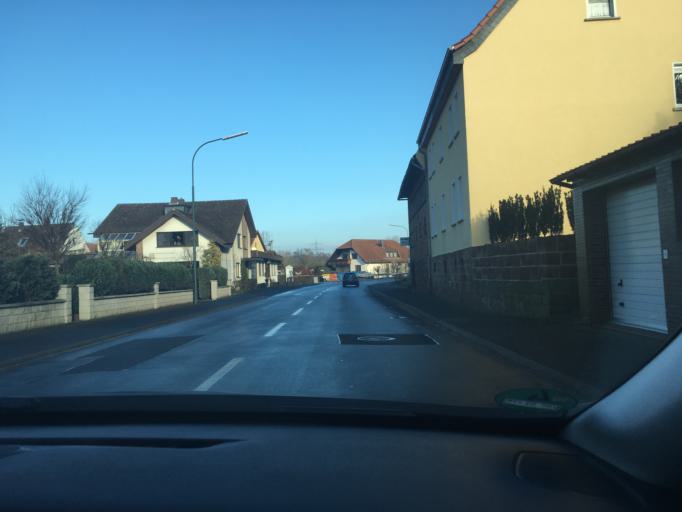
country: DE
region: Hesse
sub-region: Regierungsbezirk Kassel
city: Dipperz
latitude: 50.5672
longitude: 9.7610
